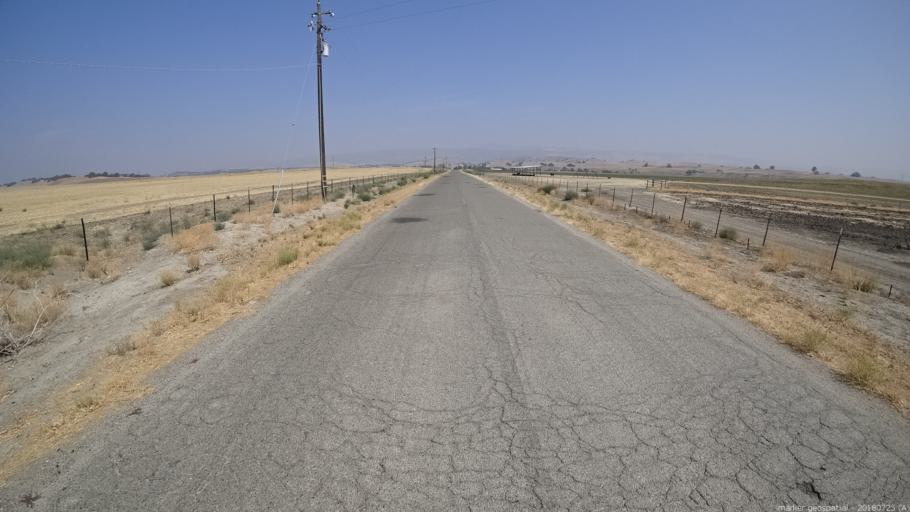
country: US
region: California
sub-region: San Luis Obispo County
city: Shandon
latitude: 35.8337
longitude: -120.3830
